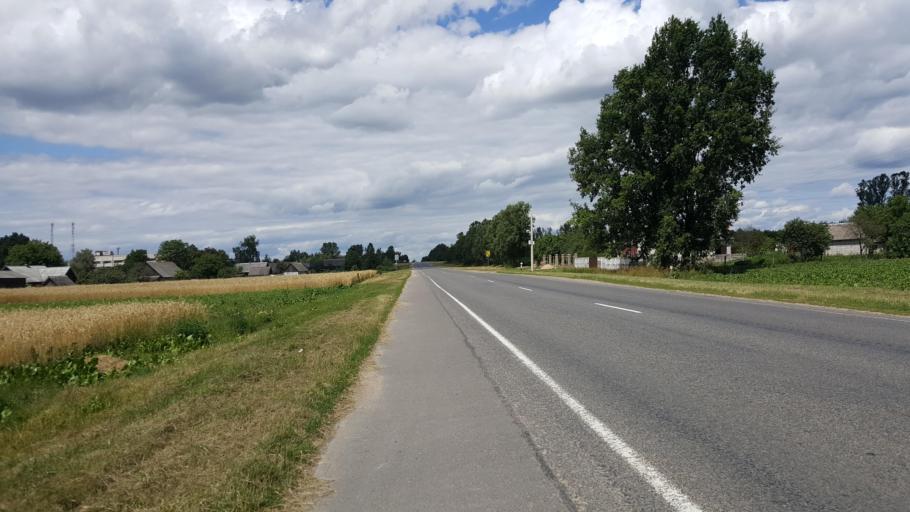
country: BY
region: Brest
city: Kamyanyets
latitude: 52.3318
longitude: 23.9136
